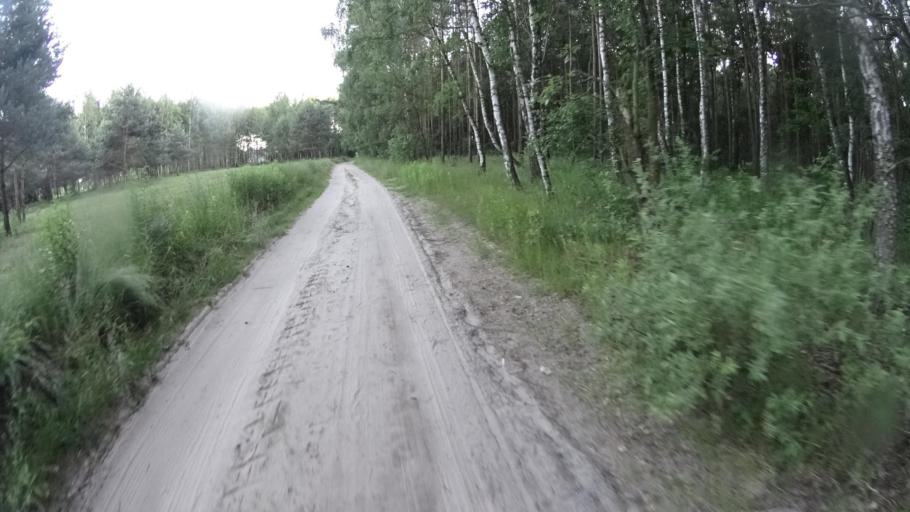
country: PL
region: Masovian Voivodeship
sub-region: Powiat warszawski zachodni
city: Jozefow
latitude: 52.2705
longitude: 20.6952
